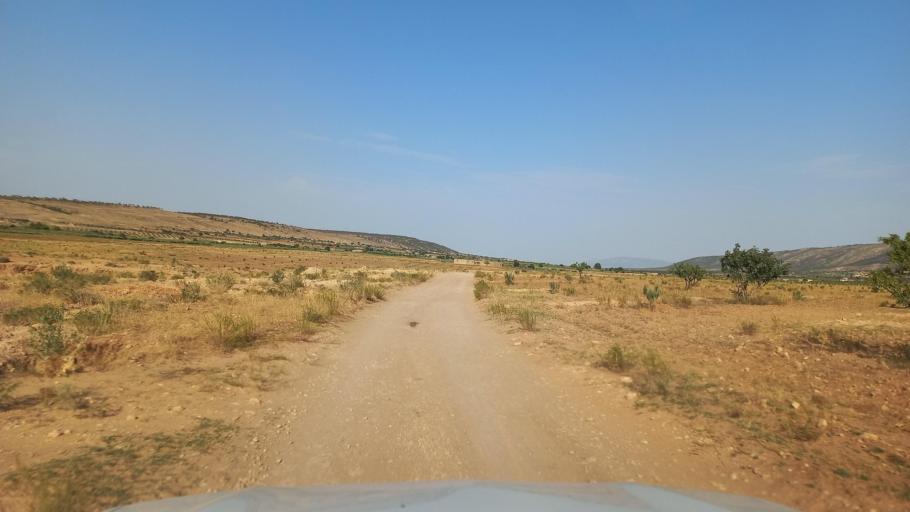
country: TN
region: Al Qasrayn
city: Kasserine
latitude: 35.3562
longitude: 8.8512
